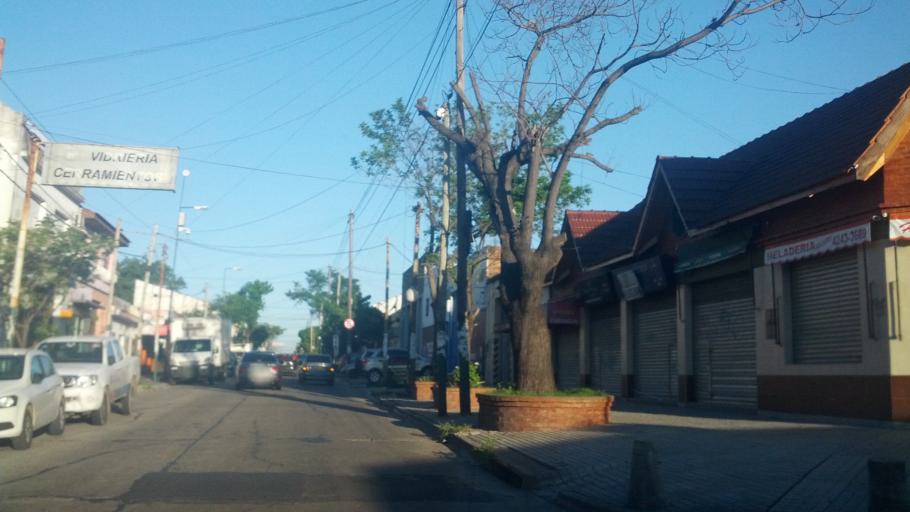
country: AR
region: Buenos Aires
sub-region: Partido de Lomas de Zamora
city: Lomas de Zamora
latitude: -34.7666
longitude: -58.4190
